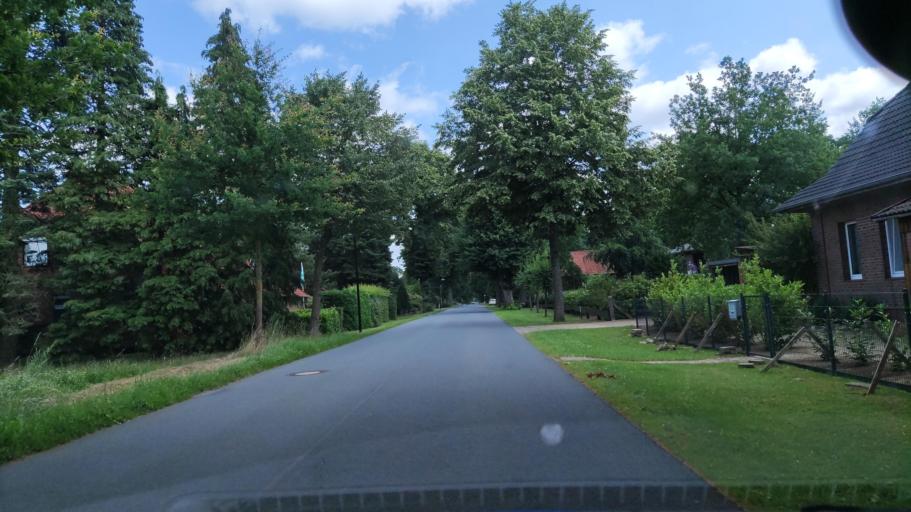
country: DE
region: Lower Saxony
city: Bad Fallingbostel
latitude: 52.8270
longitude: 9.6689
